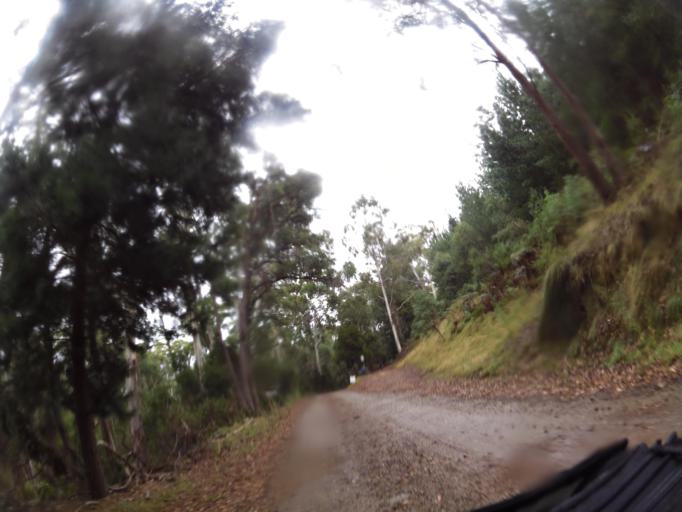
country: AU
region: New South Wales
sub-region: Greater Hume Shire
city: Holbrook
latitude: -36.1994
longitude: 147.5261
